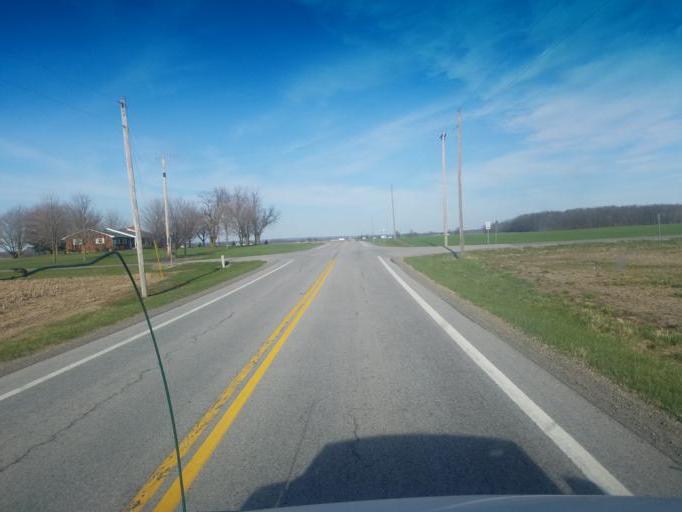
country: US
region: Ohio
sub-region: Logan County
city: De Graff
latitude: 40.3380
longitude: -83.9809
